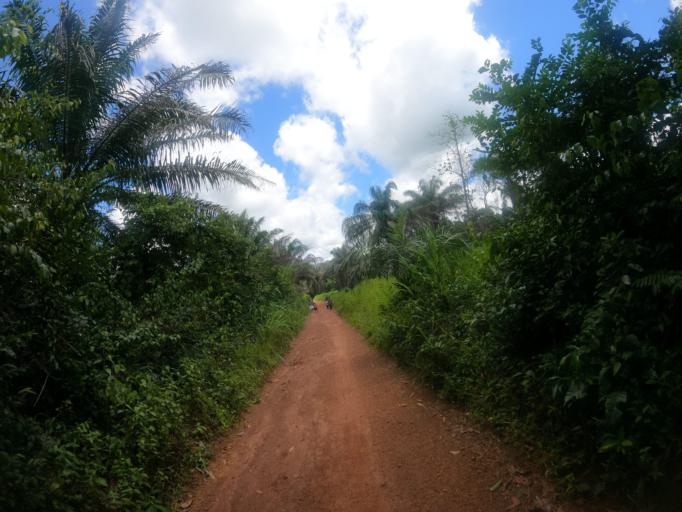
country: SL
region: Northern Province
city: Makeni
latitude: 8.8654
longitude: -12.1053
